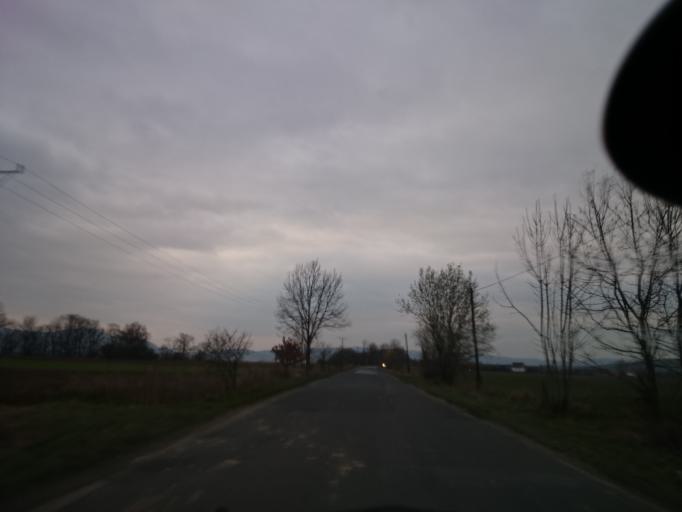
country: PL
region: Lower Silesian Voivodeship
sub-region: Powiat zabkowicki
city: Kamieniec Zabkowicki
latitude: 50.5276
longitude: 16.8375
